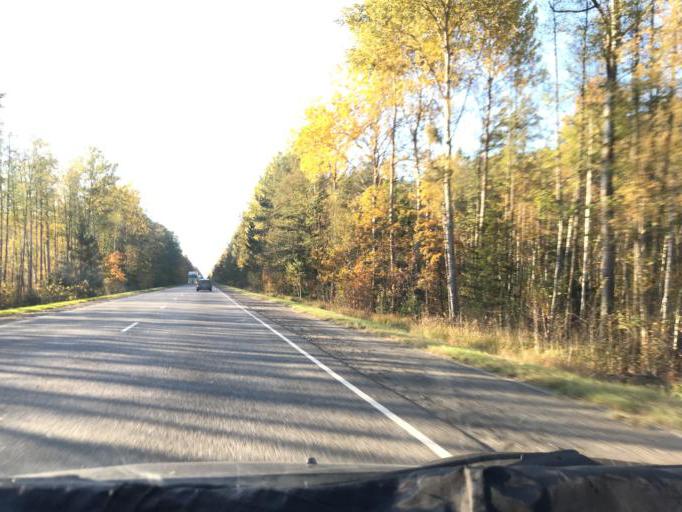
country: BY
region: Gomel
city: Pyetrykaw
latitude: 52.2615
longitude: 28.3233
